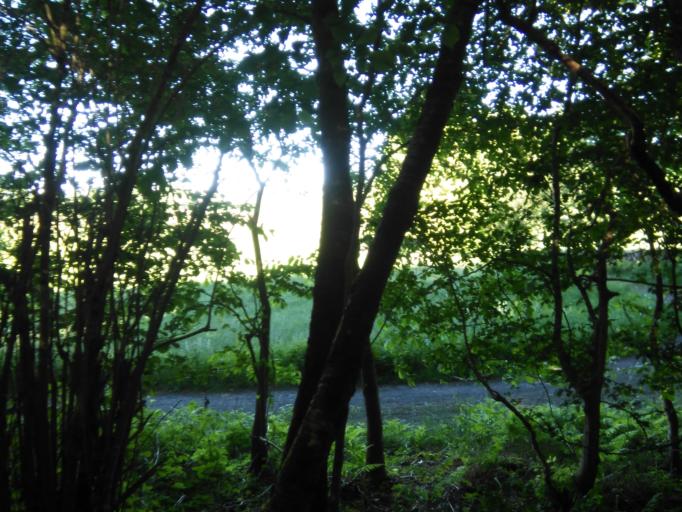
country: DK
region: Capital Region
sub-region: Bornholm Kommune
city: Ronne
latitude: 55.2563
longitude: 14.7714
